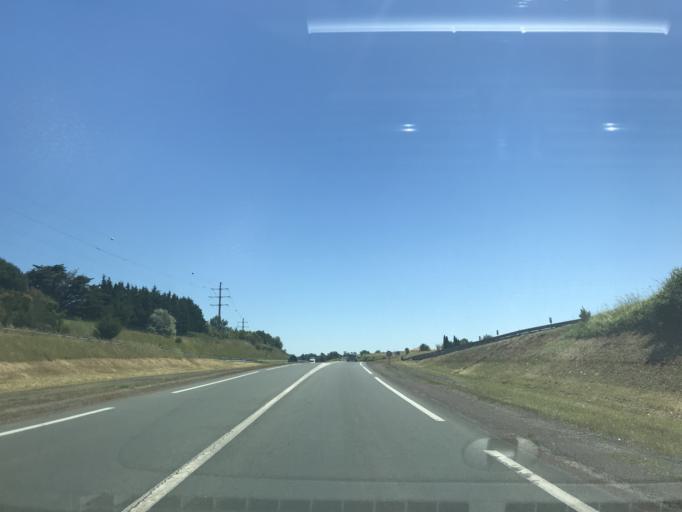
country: FR
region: Poitou-Charentes
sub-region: Departement de la Charente-Maritime
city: Saint-Georges-de-Didonne
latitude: 45.6252
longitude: -0.9986
